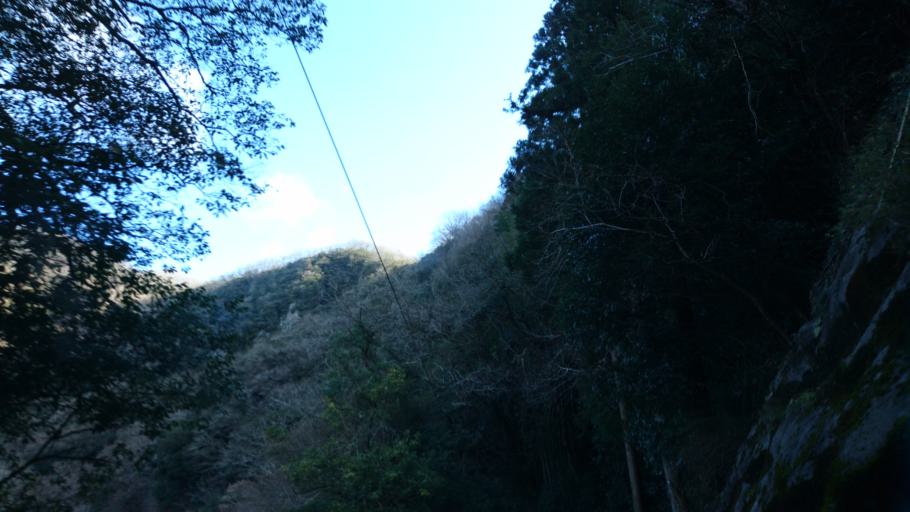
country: JP
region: Okayama
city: Takahashi
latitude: 34.8568
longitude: 133.5709
